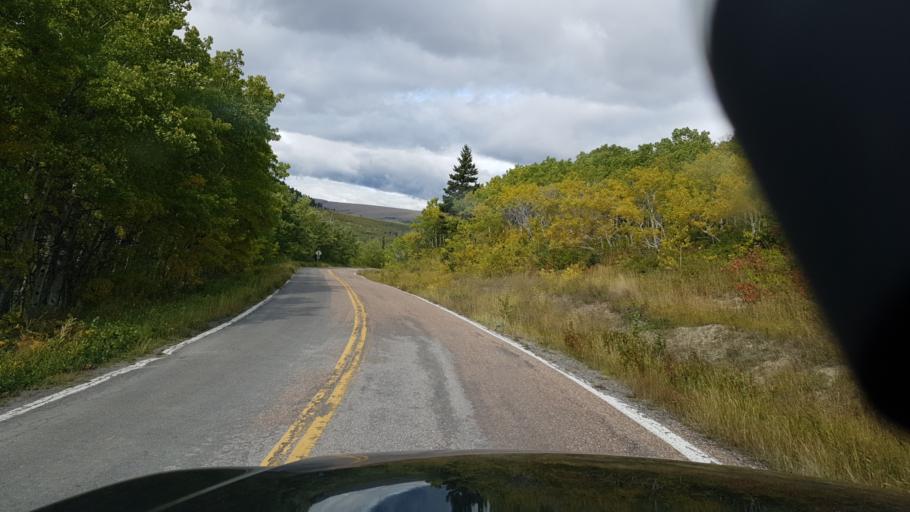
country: US
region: Montana
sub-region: Glacier County
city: South Browning
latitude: 48.5403
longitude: -113.2796
